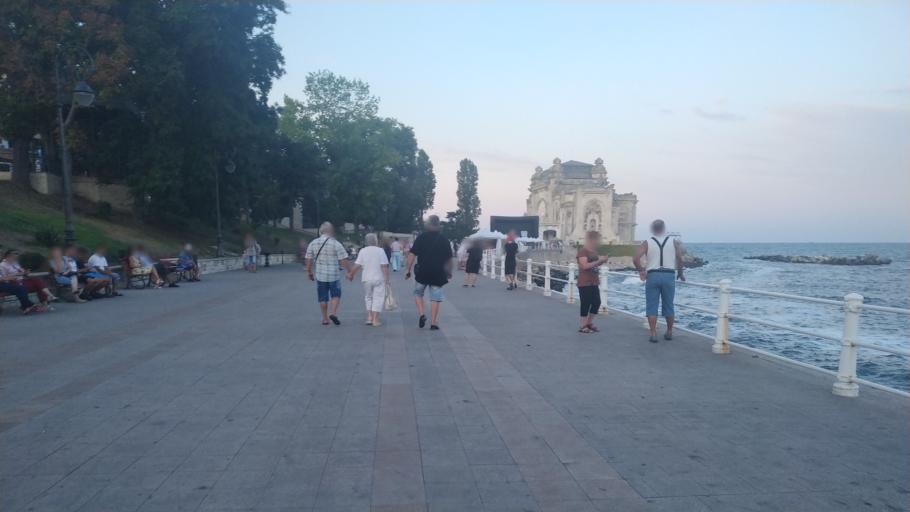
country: RO
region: Constanta
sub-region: Municipiul Constanta
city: Constanta
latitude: 44.1702
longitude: 28.6607
